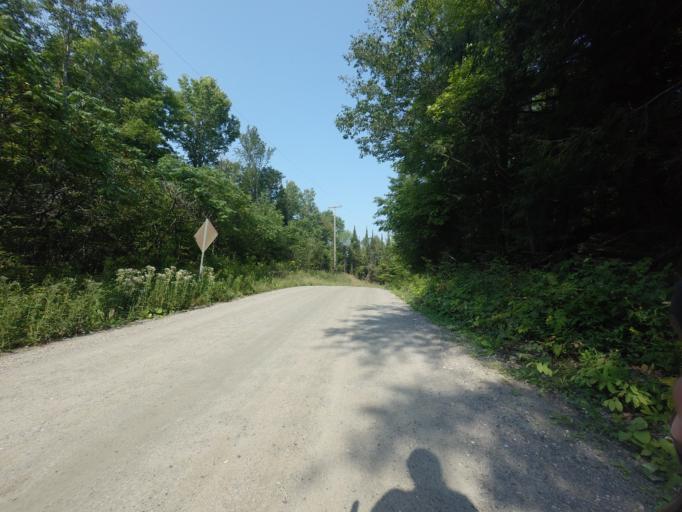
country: CA
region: Ontario
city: Perth
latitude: 44.7907
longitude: -76.7647
